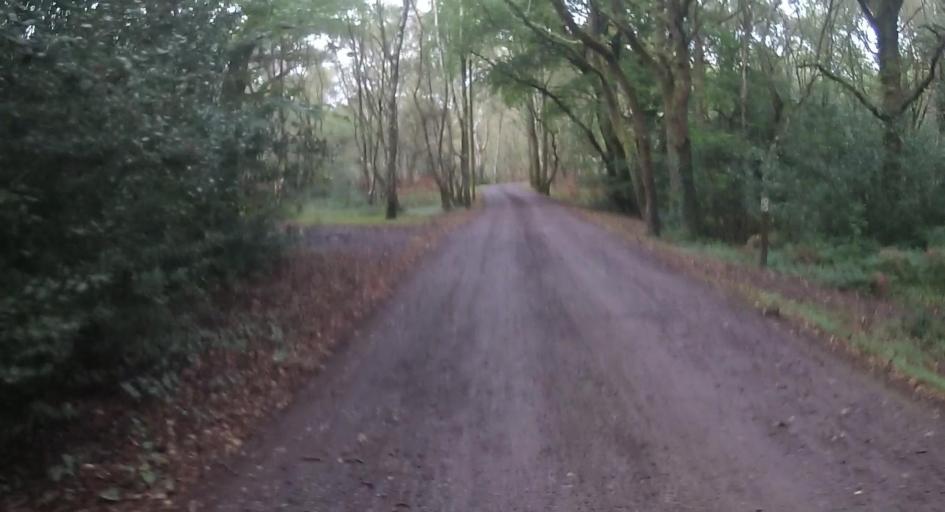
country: GB
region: England
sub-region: West Berkshire
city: Thatcham
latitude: 51.4177
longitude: -1.2290
